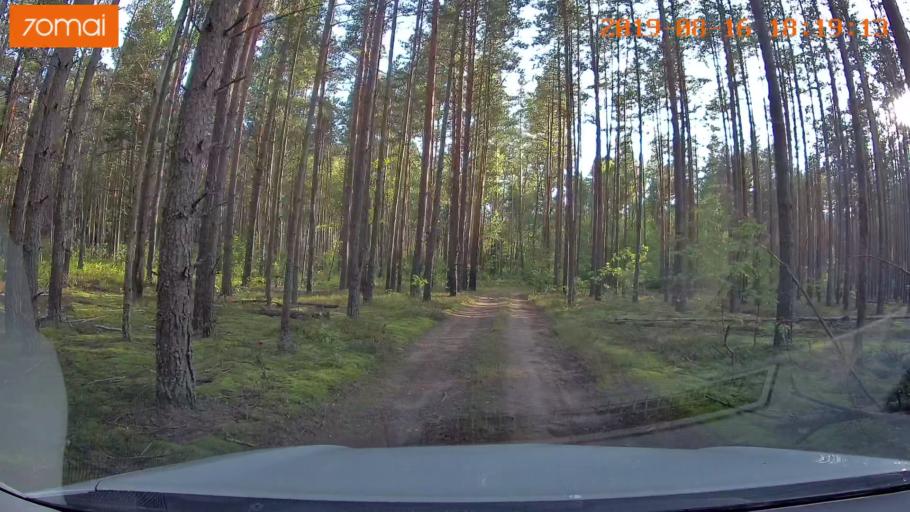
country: BY
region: Mogilev
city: Asipovichy
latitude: 53.2090
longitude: 28.6344
